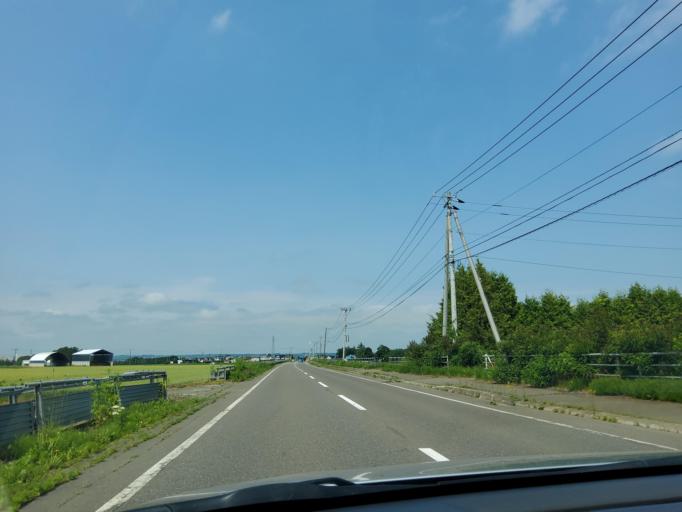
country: JP
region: Hokkaido
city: Obihiro
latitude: 42.8924
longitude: 143.0408
